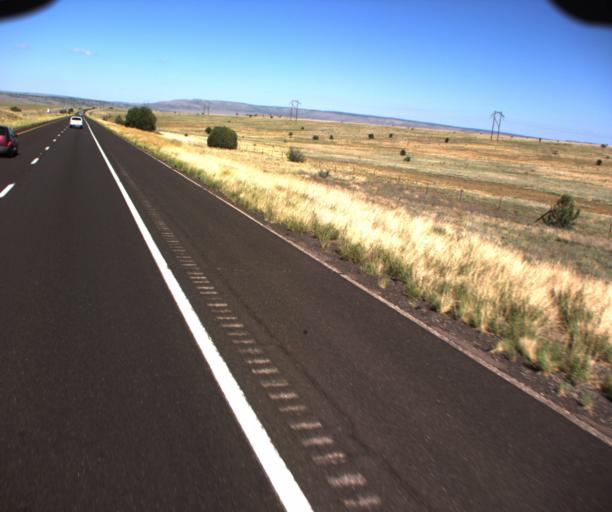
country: US
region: Arizona
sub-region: Yavapai County
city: Paulden
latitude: 35.2857
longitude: -112.8028
